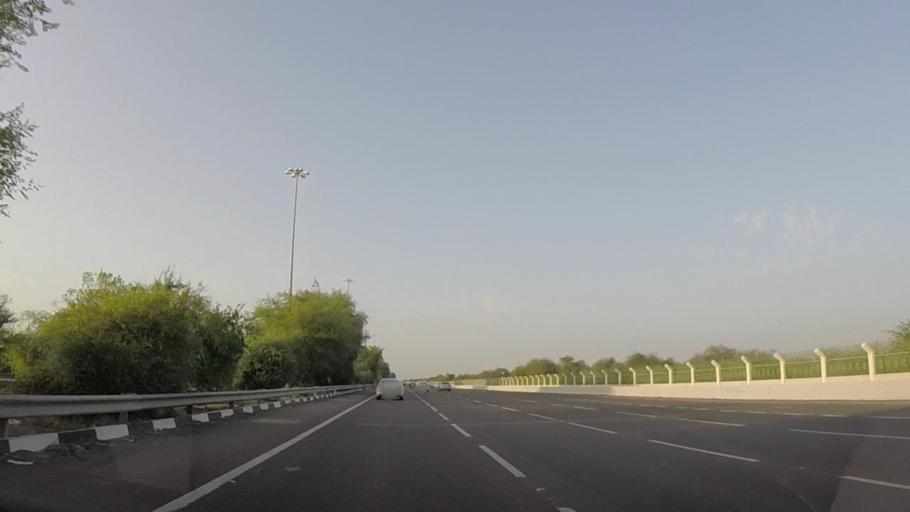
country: AE
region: Dubai
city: Dubai
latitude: 24.8580
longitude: 54.9041
